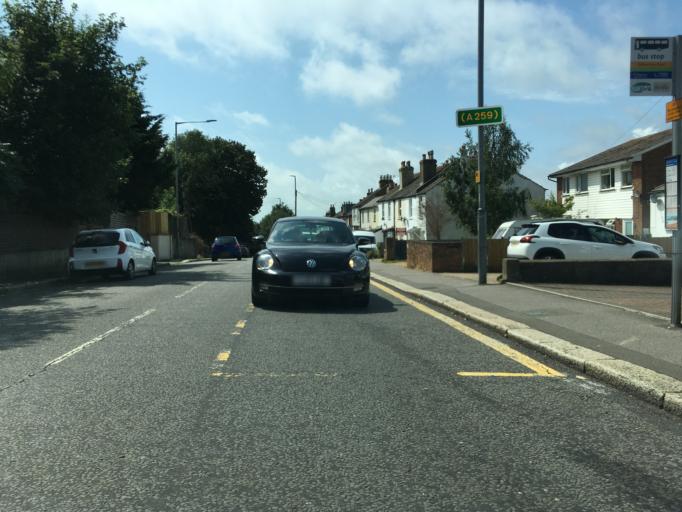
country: GB
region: England
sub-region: East Sussex
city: Hastings
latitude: 50.8701
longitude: 0.6041
